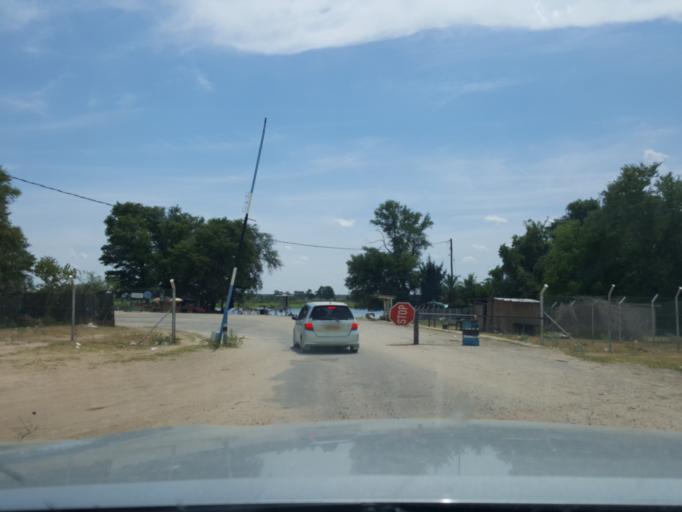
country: BW
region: North West
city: Shakawe
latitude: -18.2774
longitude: 21.7880
